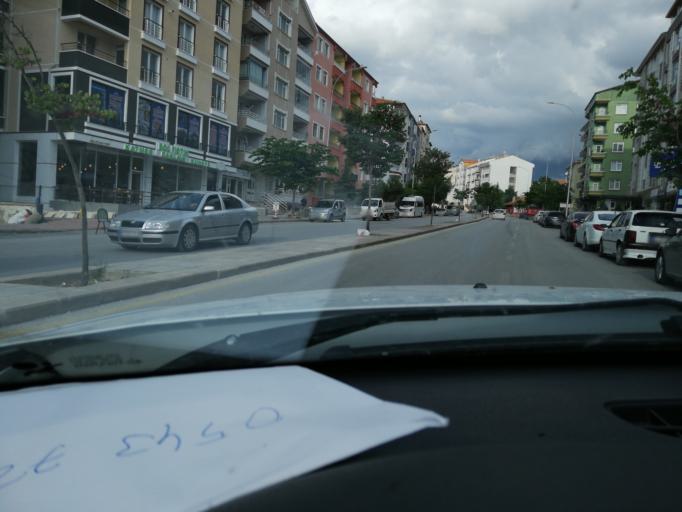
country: TR
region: Kirsehir
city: Kirsehir
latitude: 39.1399
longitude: 34.1611
